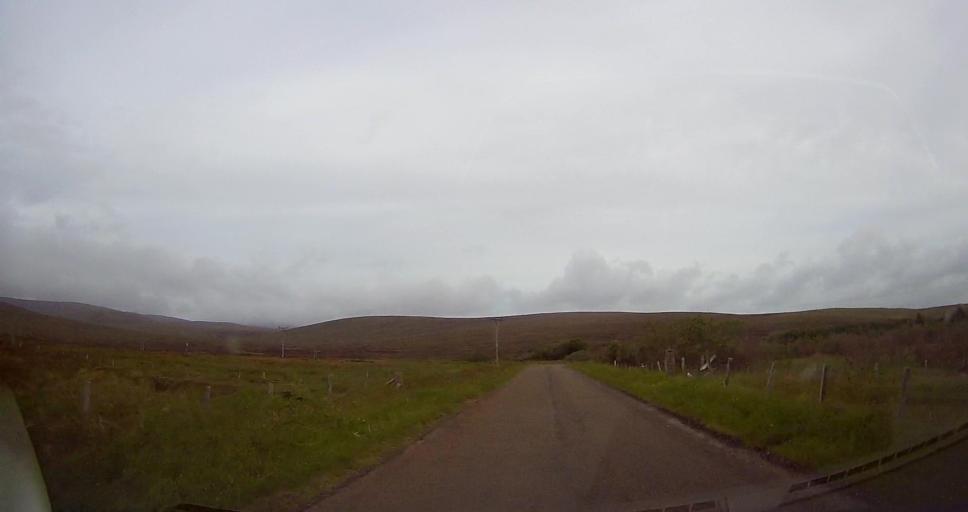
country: GB
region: Scotland
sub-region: Orkney Islands
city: Stromness
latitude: 58.8382
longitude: -3.2161
